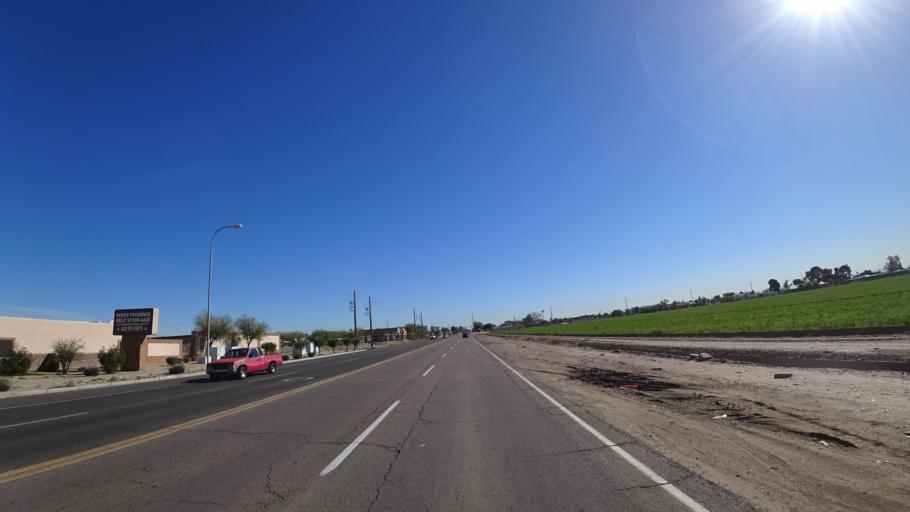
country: US
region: Arizona
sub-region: Maricopa County
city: Tolleson
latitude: 33.4941
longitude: -112.2592
